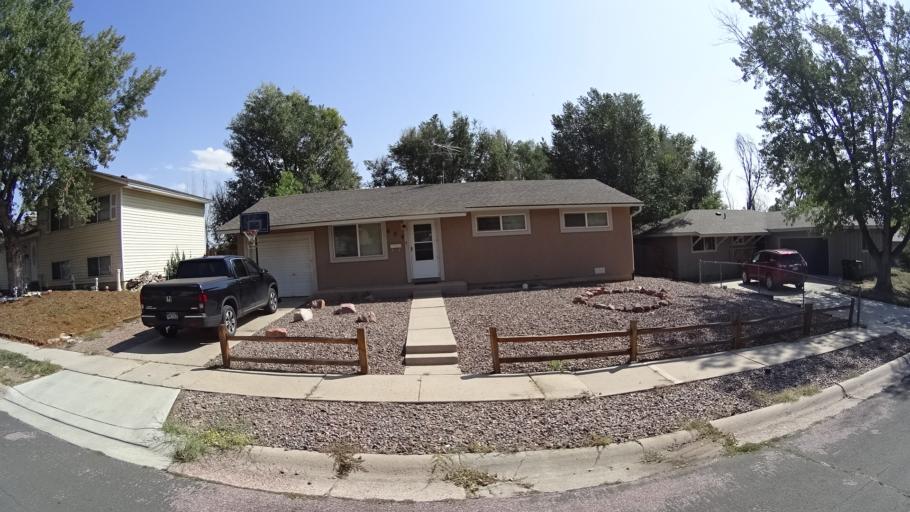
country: US
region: Colorado
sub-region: El Paso County
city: Colorado Springs
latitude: 38.8233
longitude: -104.7816
